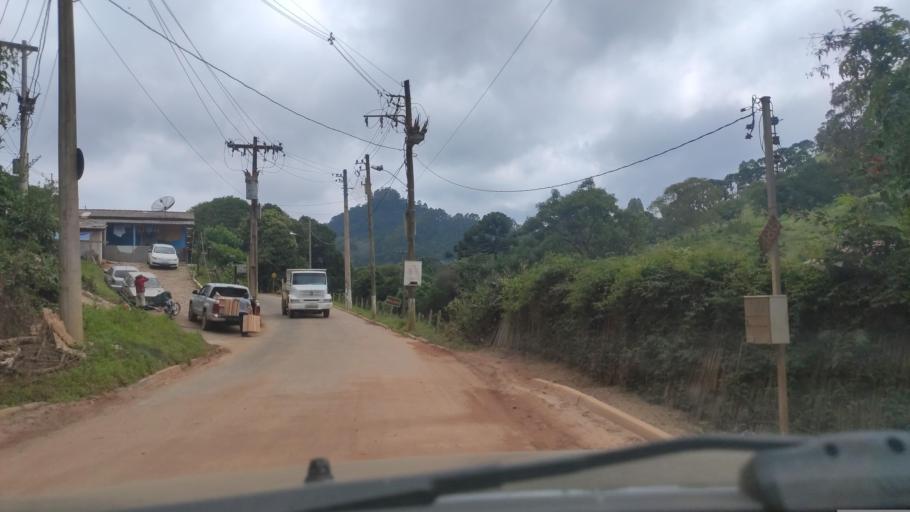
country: BR
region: Minas Gerais
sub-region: Paraisopolis
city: Paraisopolis
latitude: -22.6649
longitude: -45.8535
